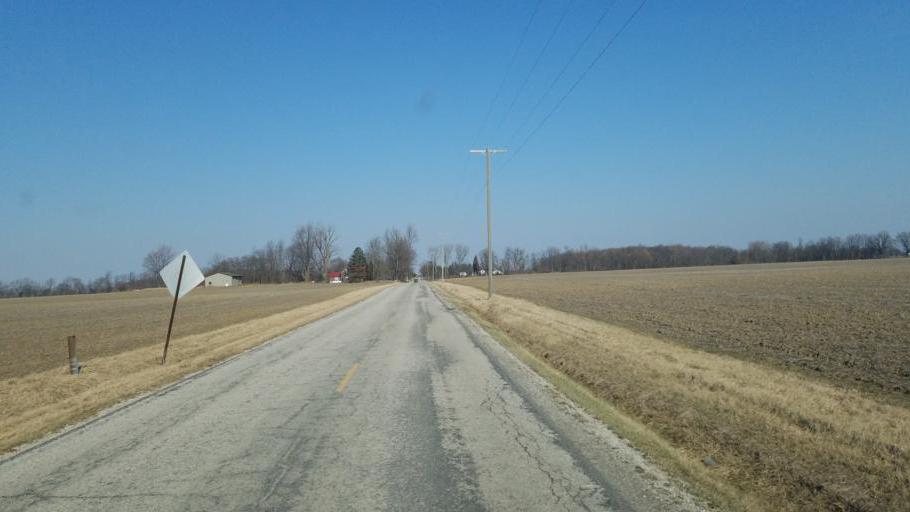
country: US
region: Ohio
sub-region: Crawford County
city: Crestline
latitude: 40.8159
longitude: -82.6968
